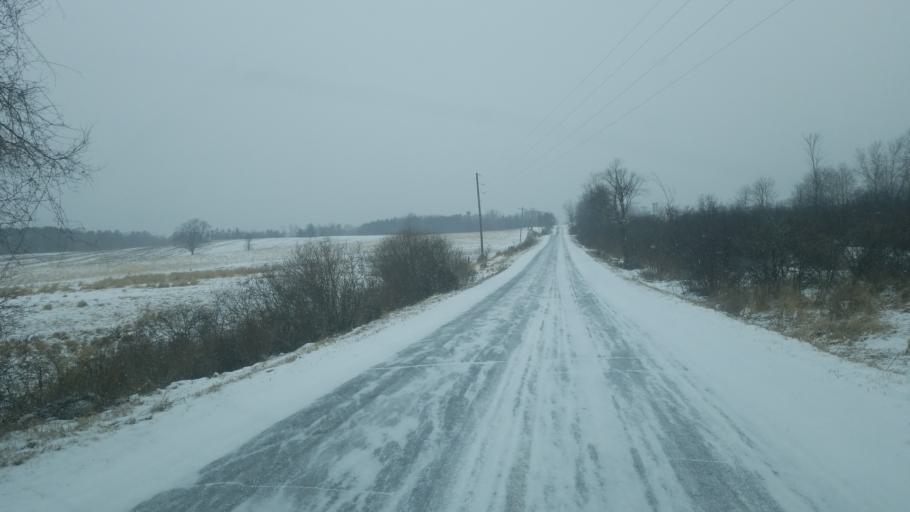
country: US
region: Michigan
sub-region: Mecosta County
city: Big Rapids
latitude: 43.7740
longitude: -85.4028
